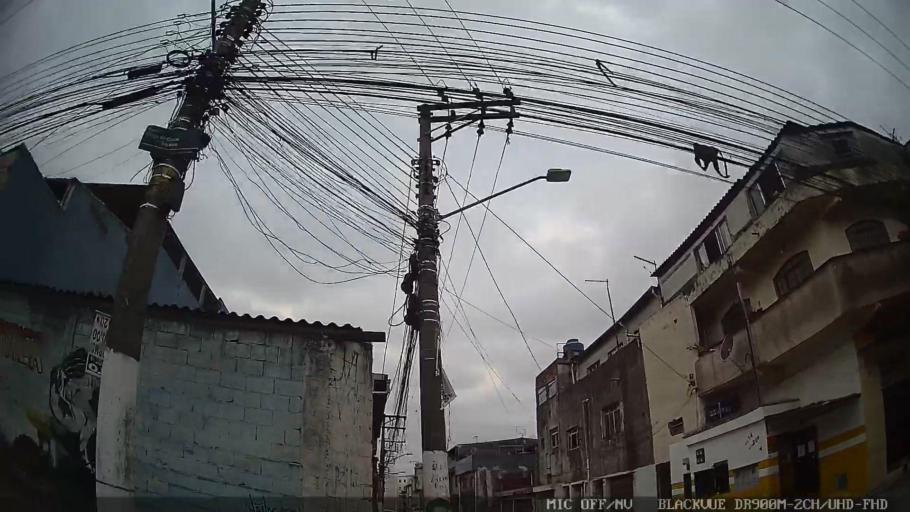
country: BR
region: Sao Paulo
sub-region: Itaquaquecetuba
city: Itaquaquecetuba
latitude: -23.4819
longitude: -46.3795
